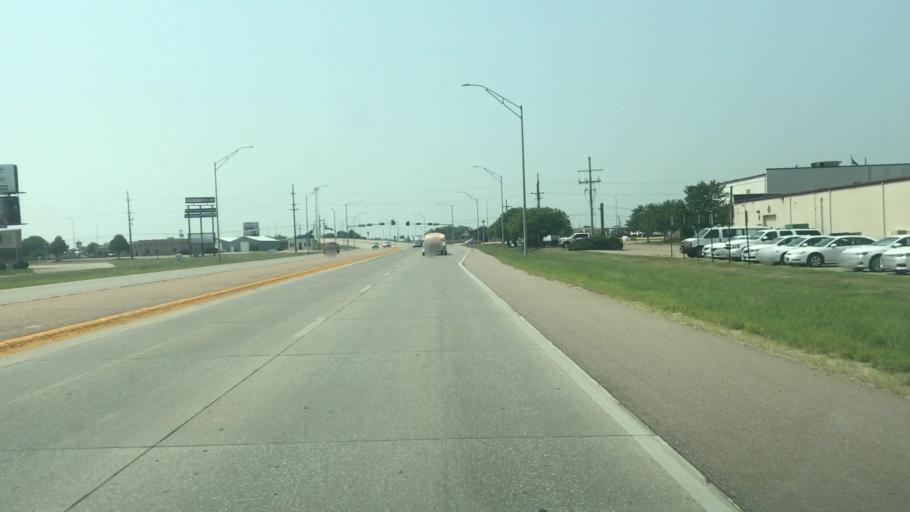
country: US
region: Nebraska
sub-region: Hall County
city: Grand Island
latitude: 40.9156
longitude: -98.3757
